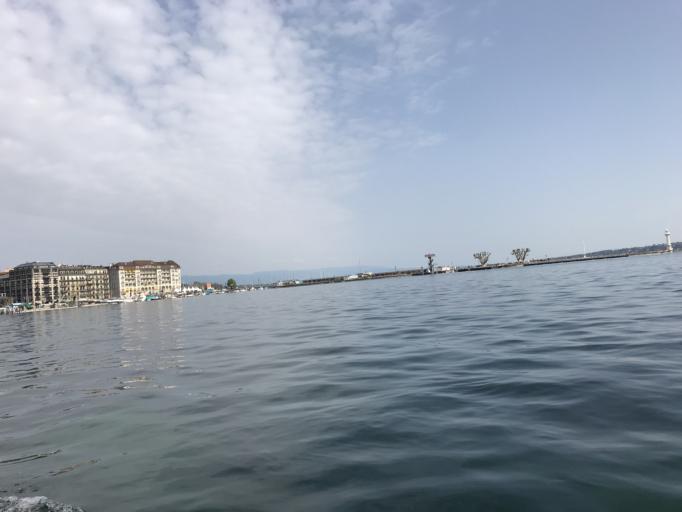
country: CH
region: Geneva
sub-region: Geneva
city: Geneve
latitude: 46.2071
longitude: 6.1527
